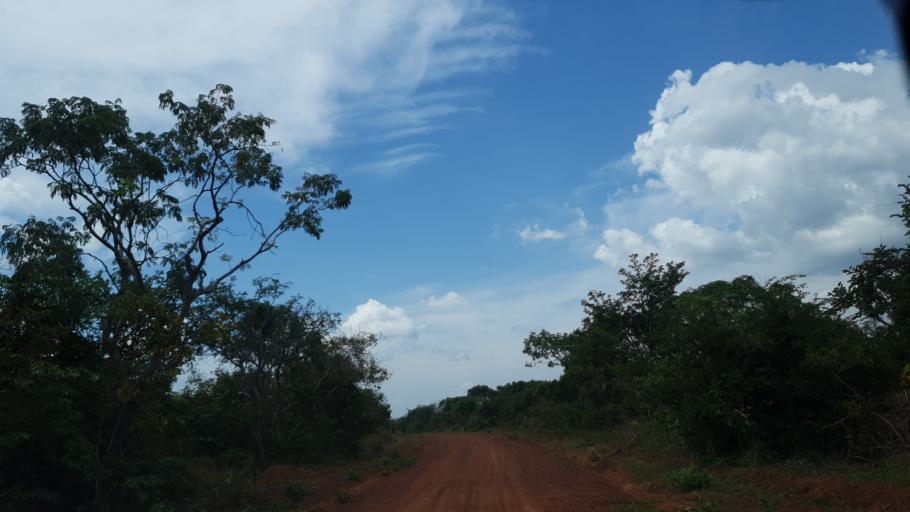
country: ML
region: Sikasso
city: Sikasso
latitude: 11.6850
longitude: -6.2061
